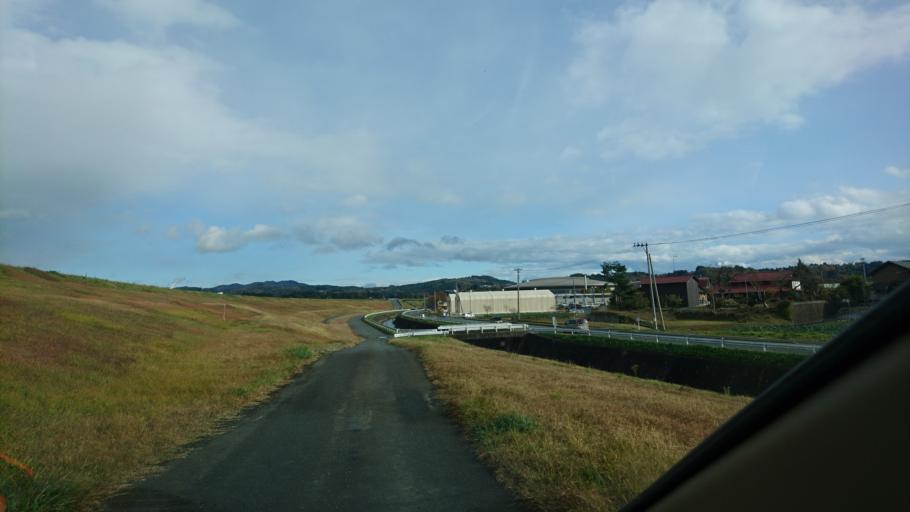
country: JP
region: Iwate
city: Ichinoseki
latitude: 38.9432
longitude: 141.1508
